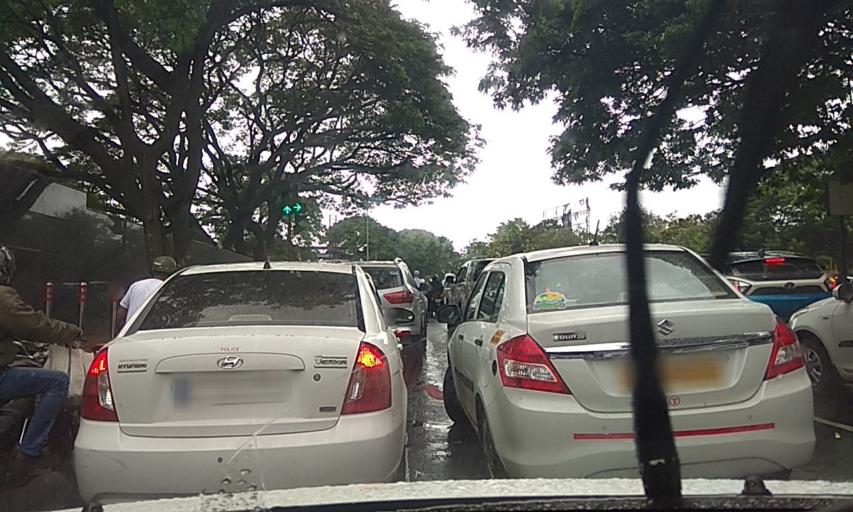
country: IN
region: Maharashtra
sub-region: Pune Division
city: Khadki
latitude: 18.5526
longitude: 73.8901
